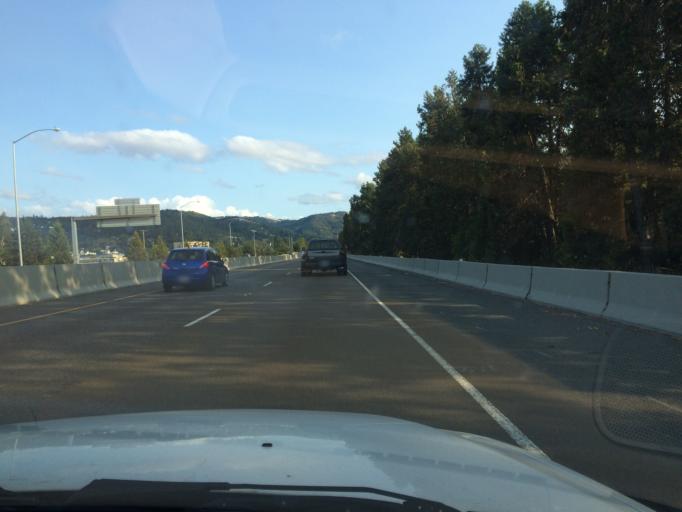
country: US
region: Oregon
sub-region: Douglas County
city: Roseburg
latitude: 43.2182
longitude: -123.3576
